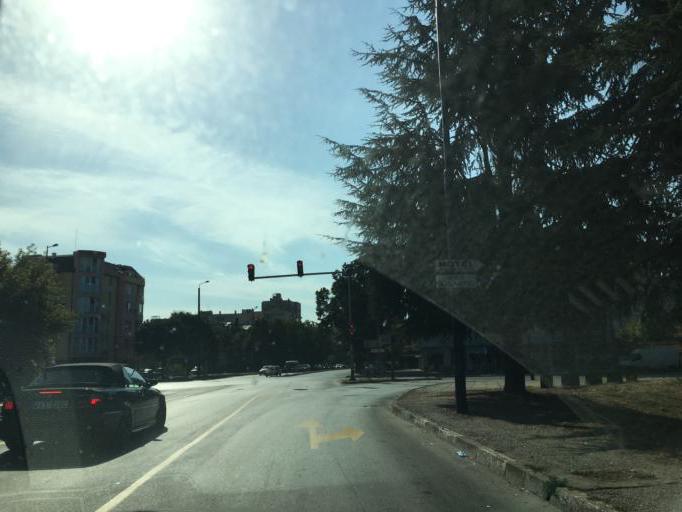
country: BG
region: Pazardzhik
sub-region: Obshtina Pazardzhik
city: Pazardzhik
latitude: 42.2071
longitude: 24.3281
